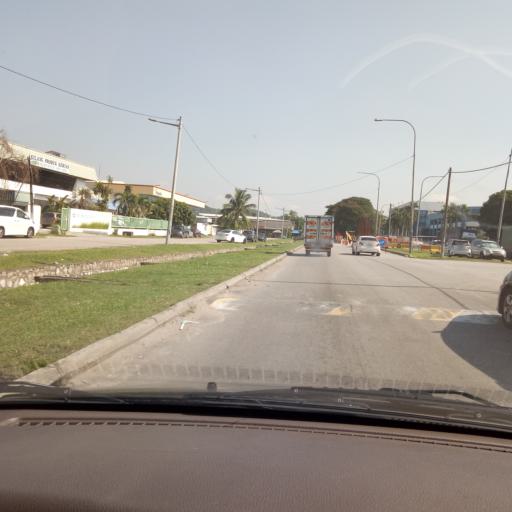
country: MY
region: Selangor
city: Kampong Baharu Balakong
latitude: 3.0237
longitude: 101.7649
